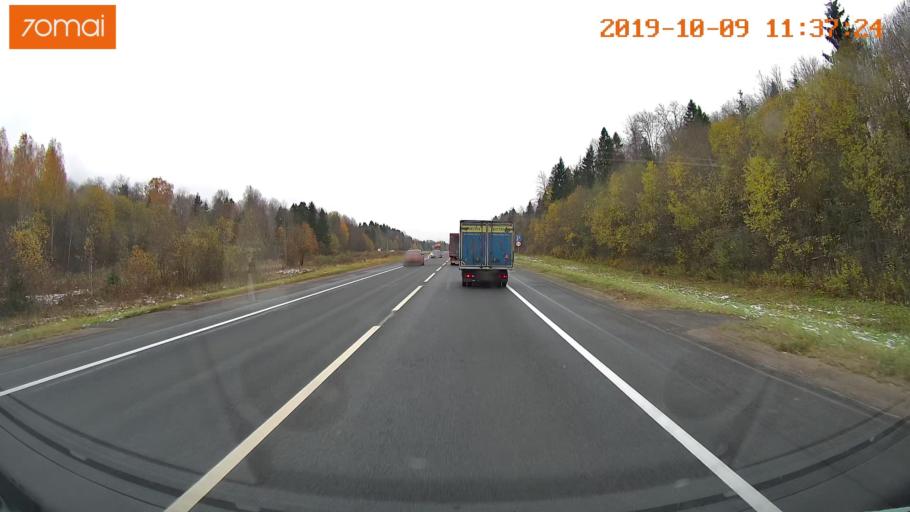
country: RU
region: Vologda
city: Gryazovets
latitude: 58.9797
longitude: 40.1461
